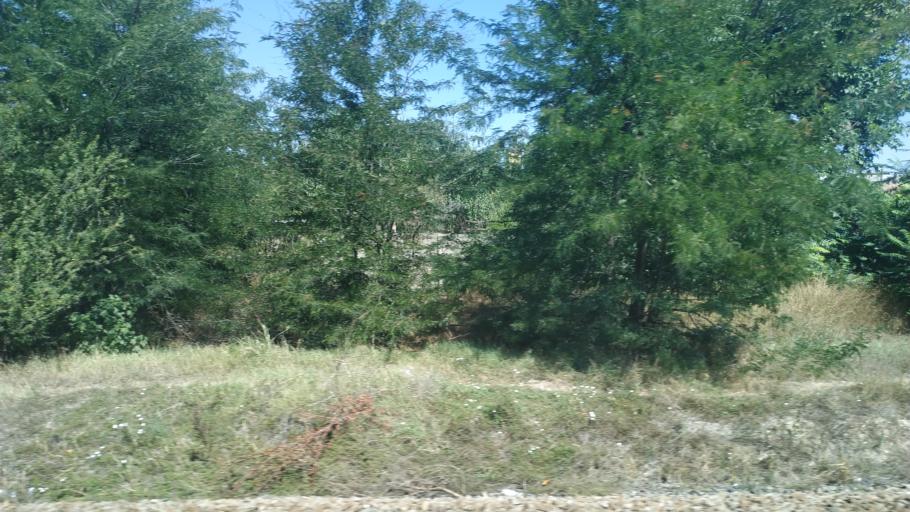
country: RO
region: Constanta
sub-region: Oras Murfatlar
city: Murfatlar
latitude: 44.1732
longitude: 28.4074
